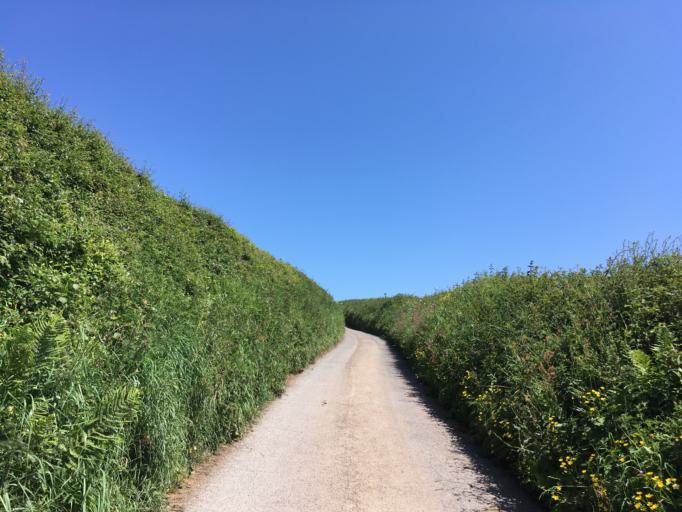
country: GB
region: England
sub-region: Devon
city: Dartmouth
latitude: 50.3470
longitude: -3.5434
